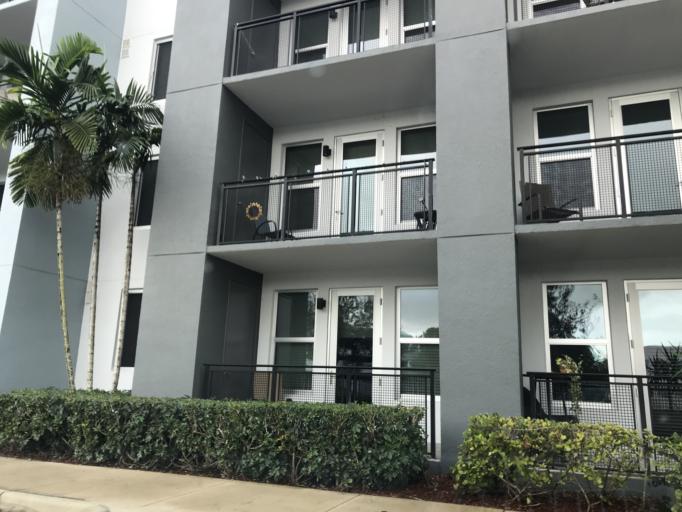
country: US
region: Florida
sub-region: Palm Beach County
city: Delray Beach
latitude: 26.4554
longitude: -80.0953
